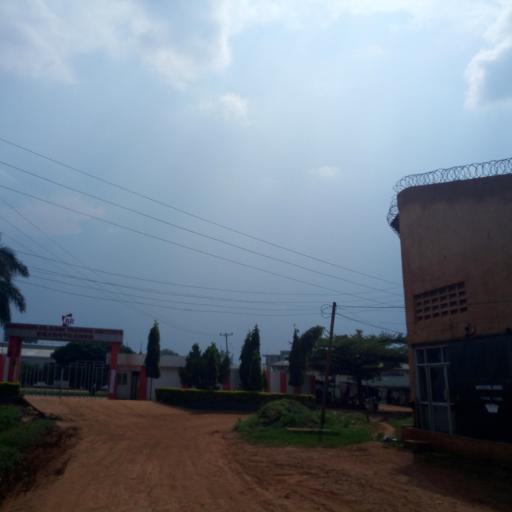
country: UG
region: Central Region
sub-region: Kampala District
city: Kampala
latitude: 0.3156
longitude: 32.6158
